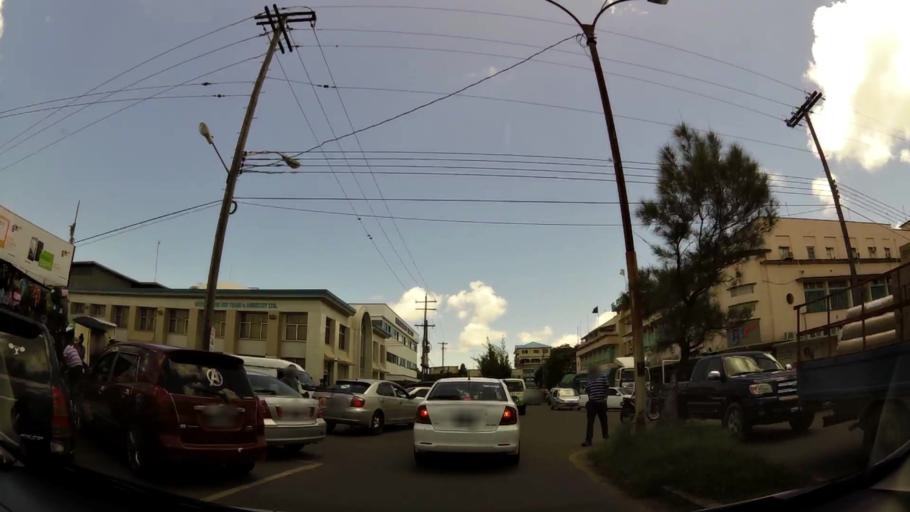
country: GY
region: Demerara-Mahaica
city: Georgetown
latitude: 6.8126
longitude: -58.1668
